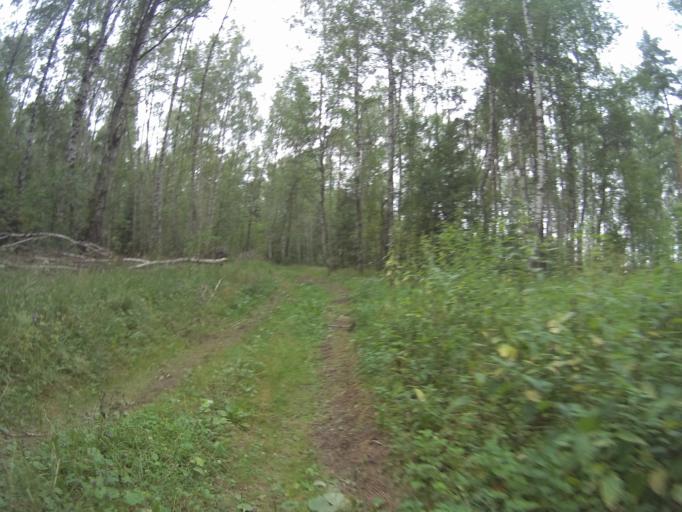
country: RU
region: Vladimir
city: Raduzhnyy
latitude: 55.9913
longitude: 40.2175
